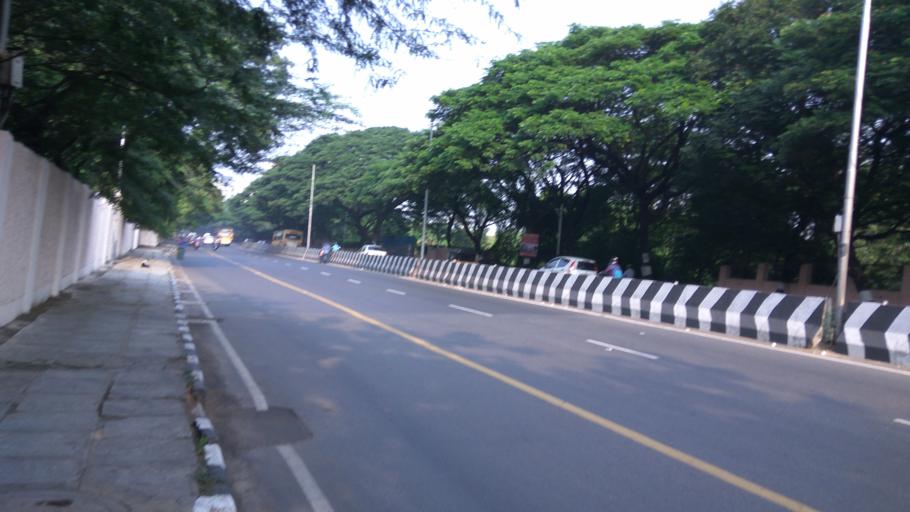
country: IN
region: Tamil Nadu
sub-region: Kancheepuram
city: Alandur
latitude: 13.0095
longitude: 80.2274
